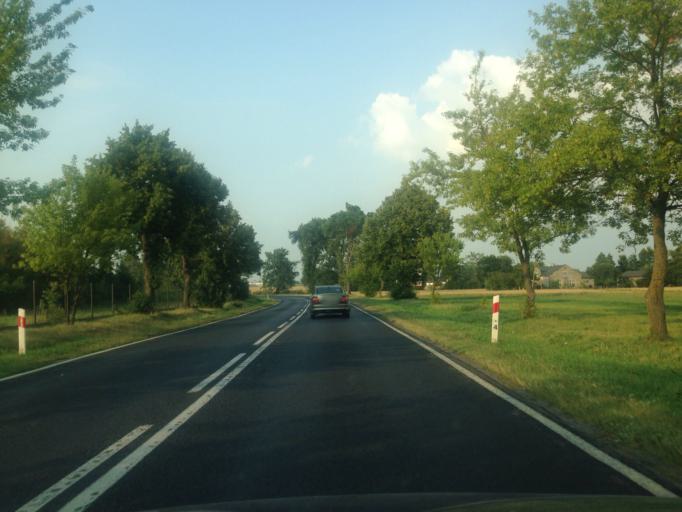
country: PL
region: Kujawsko-Pomorskie
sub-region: Powiat lipnowski
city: Lipno
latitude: 52.8197
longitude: 19.1508
